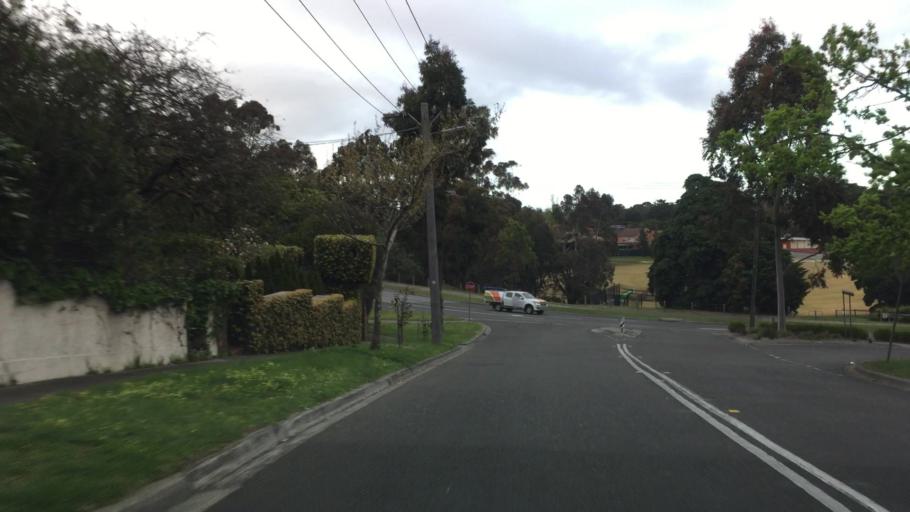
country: AU
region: Victoria
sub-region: Stonnington
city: Glen Iris
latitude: -37.8597
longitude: 145.0636
